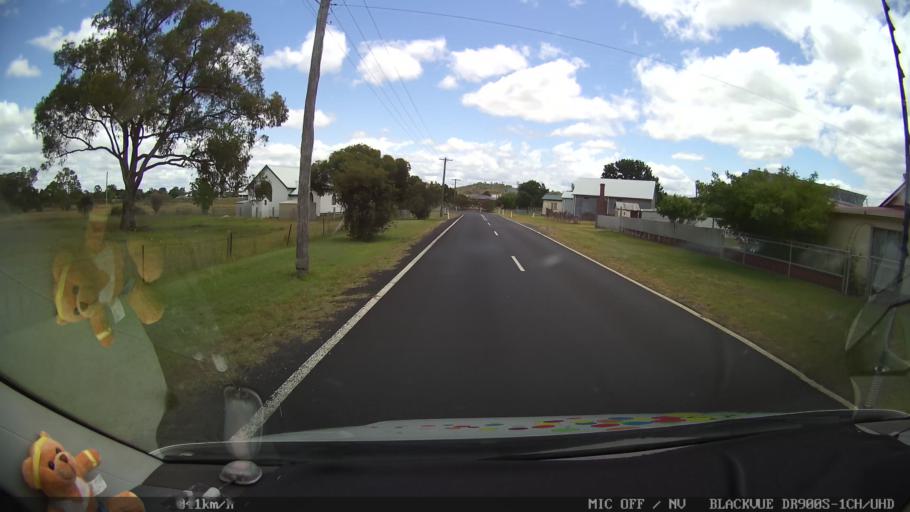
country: AU
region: New South Wales
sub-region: Glen Innes Severn
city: Glen Innes
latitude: -29.4475
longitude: 151.5984
